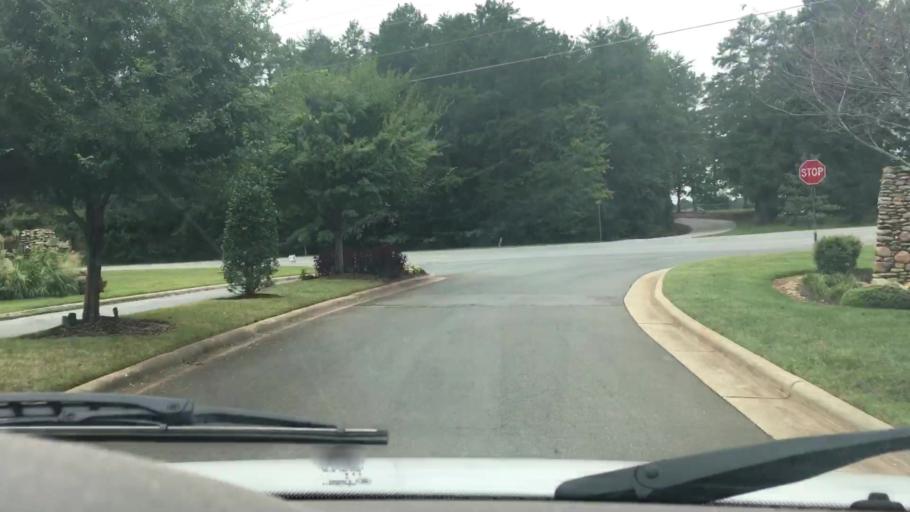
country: US
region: North Carolina
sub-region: Gaston County
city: Davidson
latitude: 35.5177
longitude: -80.7988
